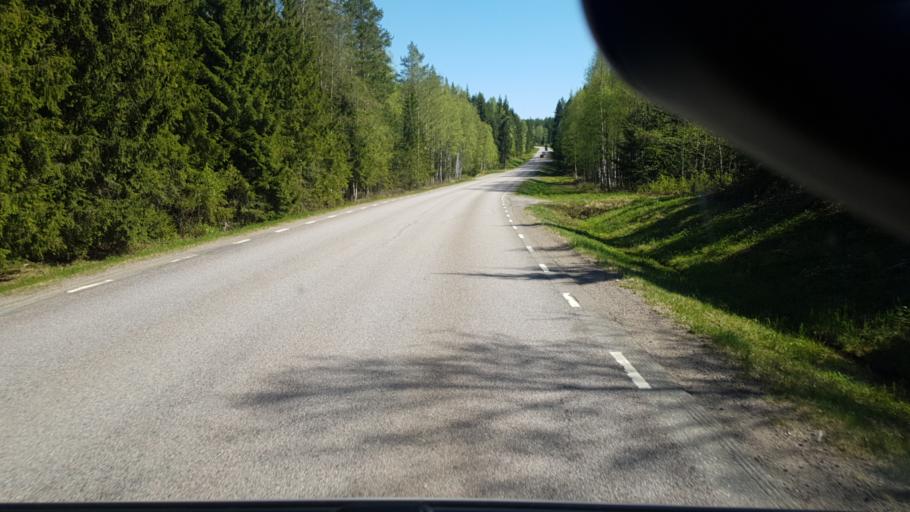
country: SE
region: Vaermland
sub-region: Eda Kommun
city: Charlottenberg
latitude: 59.8837
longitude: 12.3664
